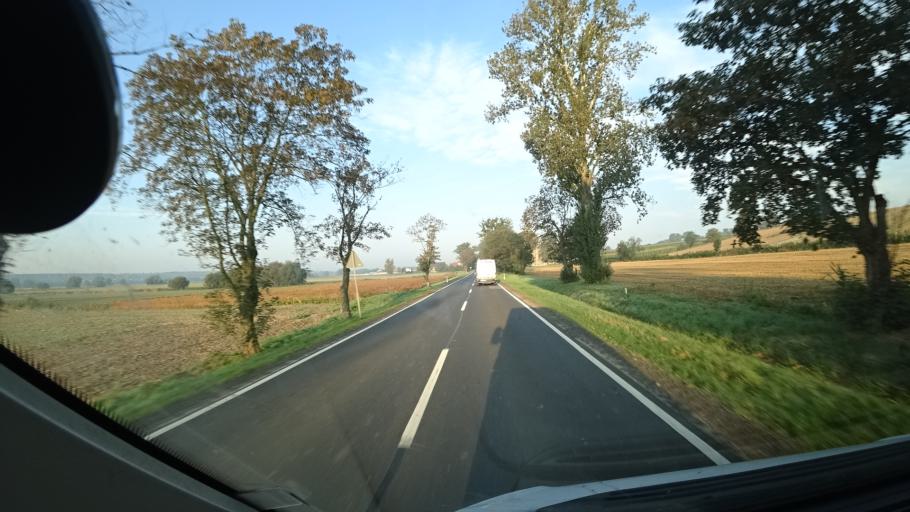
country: PL
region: Opole Voivodeship
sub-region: Powiat strzelecki
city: Ujazd
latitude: 50.3869
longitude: 18.3703
